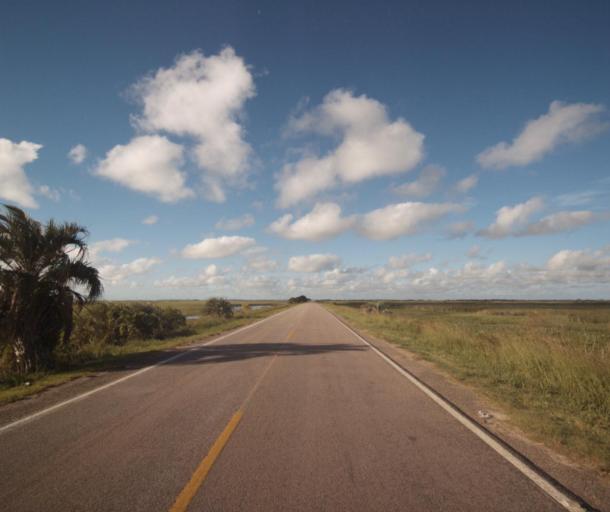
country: BR
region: Rio Grande do Sul
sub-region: Arroio Grande
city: Arroio Grande
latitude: -32.6096
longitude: -52.5727
